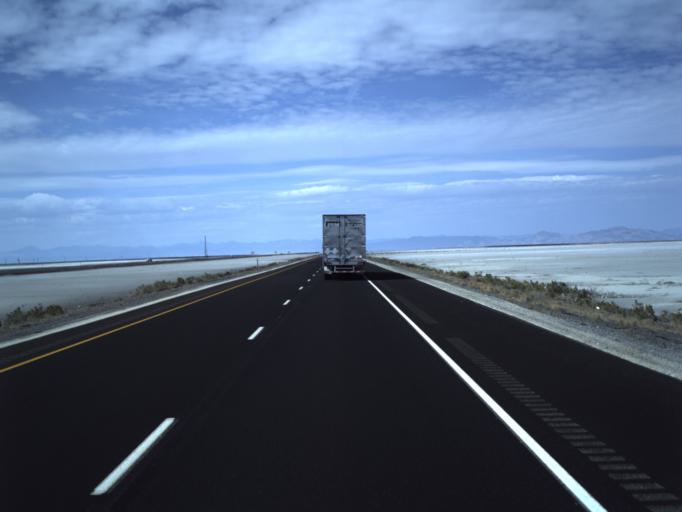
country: US
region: Utah
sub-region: Tooele County
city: Wendover
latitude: 40.7323
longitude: -113.5196
